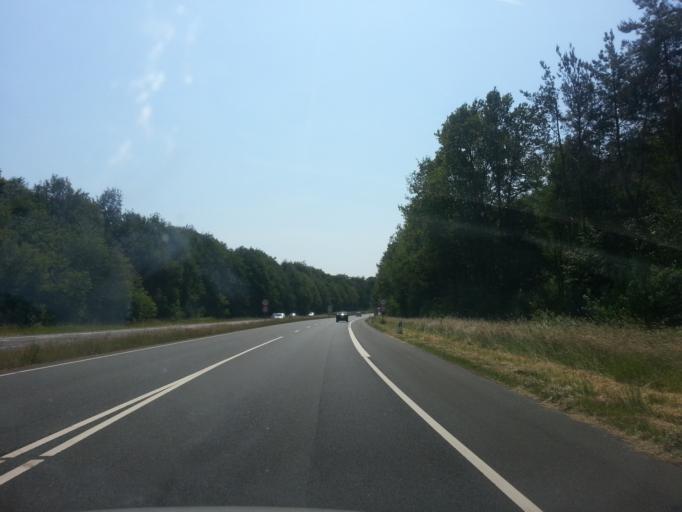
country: DE
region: Hesse
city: Dreieich
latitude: 50.0321
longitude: 8.7144
